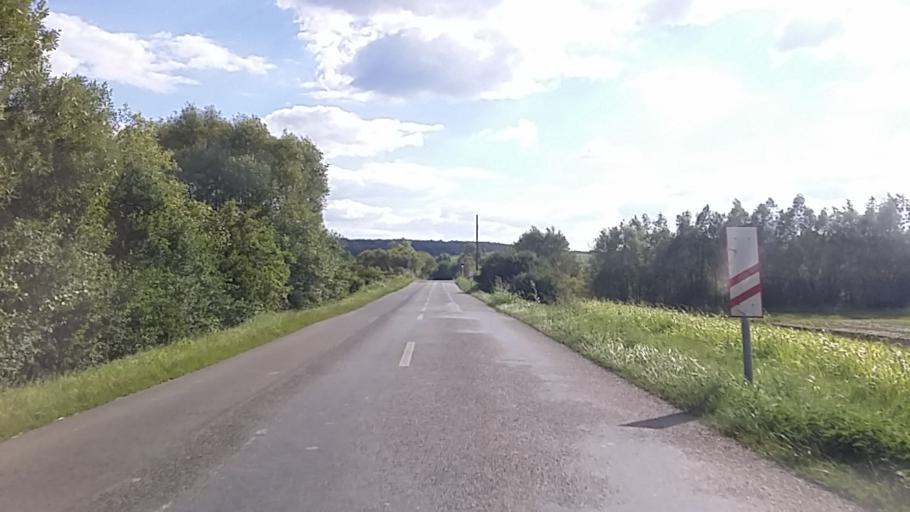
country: HU
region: Baranya
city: Sasd
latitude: 46.2177
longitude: 18.1077
